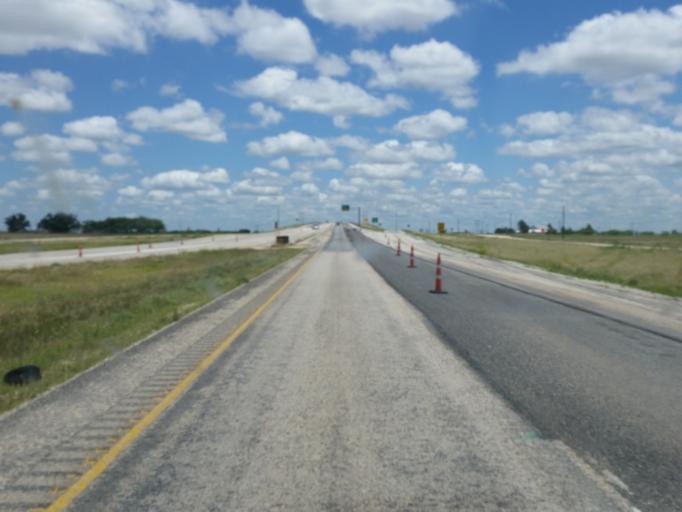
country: US
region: Texas
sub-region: Nolan County
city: Roscoe
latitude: 32.4529
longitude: -100.5268
